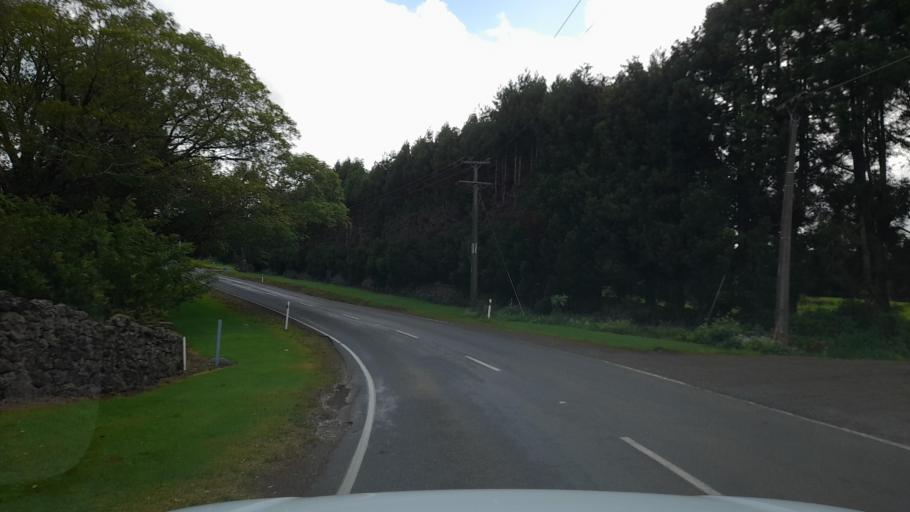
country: NZ
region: Northland
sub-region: Whangarei
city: Maungatapere
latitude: -35.7434
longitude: 174.2582
